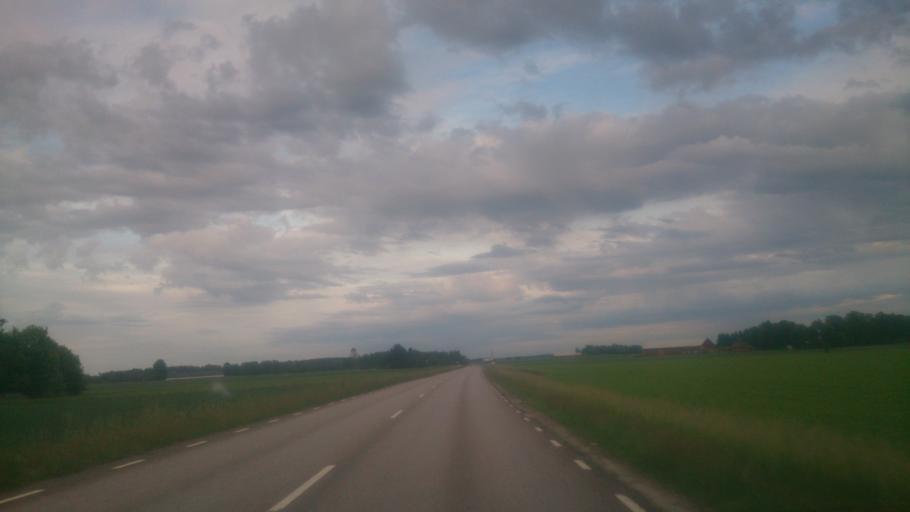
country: SE
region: OEstergoetland
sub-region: Motala Kommun
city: Borensberg
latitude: 58.4930
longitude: 15.3527
